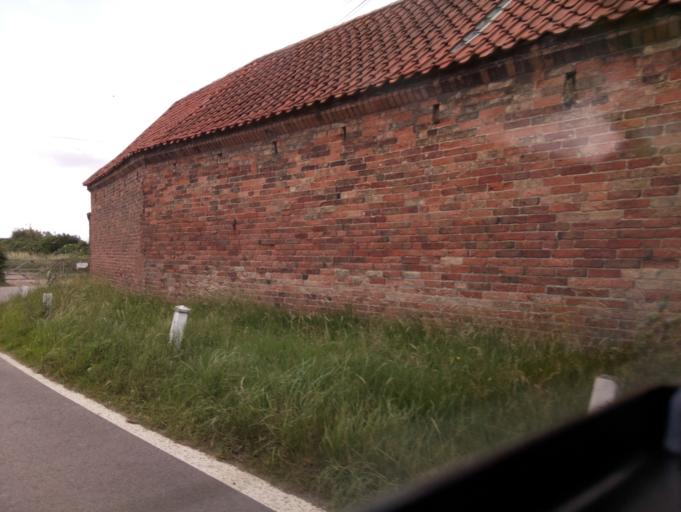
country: GB
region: England
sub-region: Nottinghamshire
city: Radcliffe on Trent
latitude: 52.9303
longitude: -1.0798
